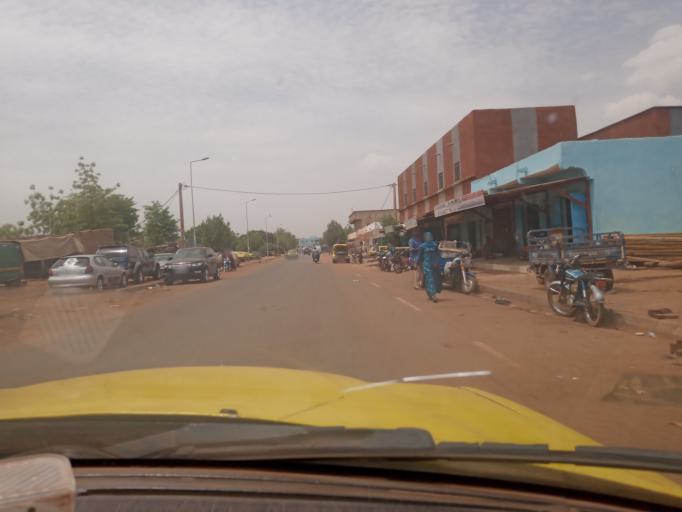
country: ML
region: Bamako
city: Bamako
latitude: 12.5937
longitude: -7.9539
